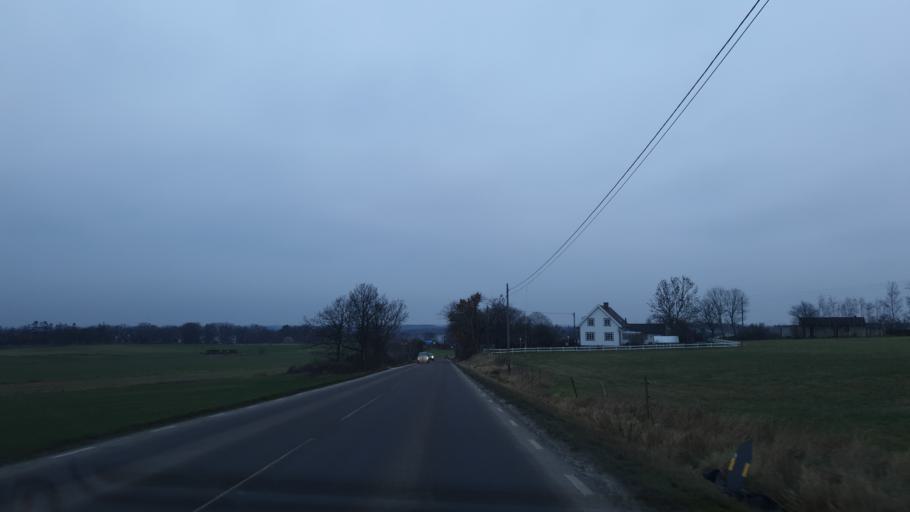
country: SE
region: Blekinge
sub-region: Karlskrona Kommun
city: Sturko
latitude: 56.1328
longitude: 15.7398
